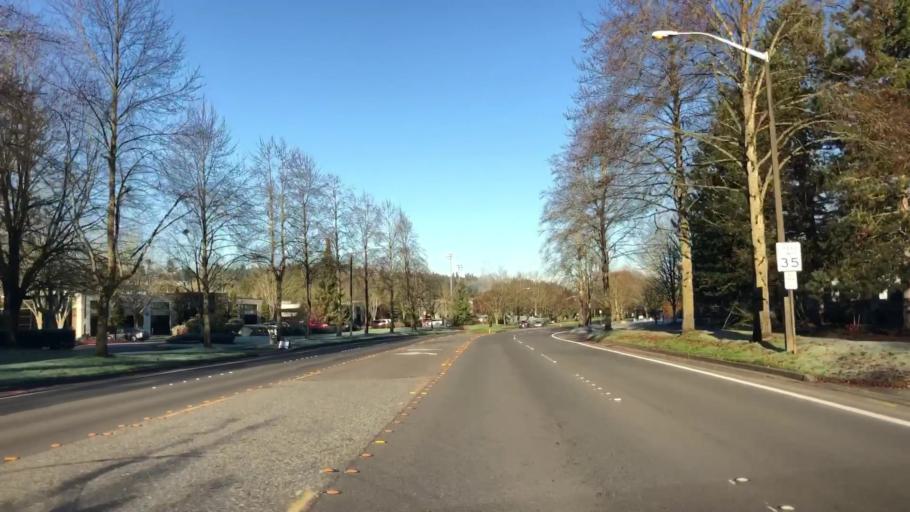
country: US
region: Washington
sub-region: King County
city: Woodinville
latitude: 47.7643
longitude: -122.1776
